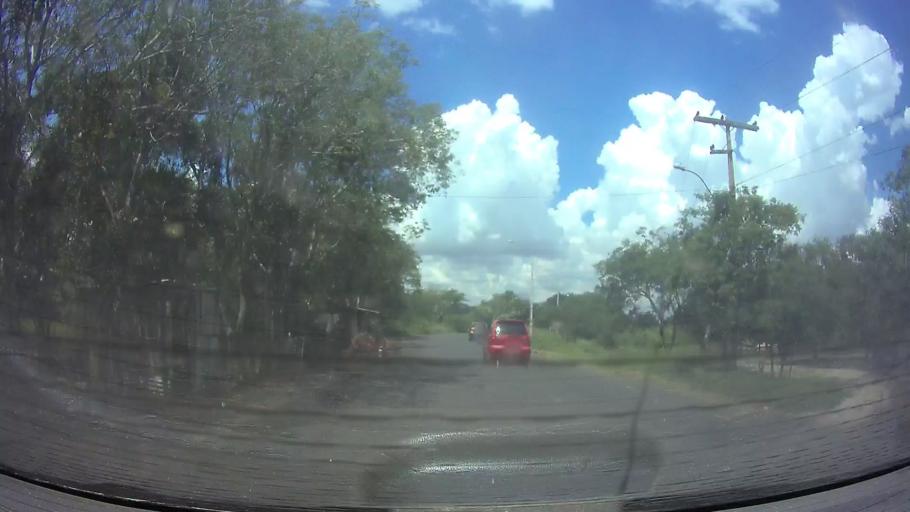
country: PY
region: Presidente Hayes
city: Nanawa
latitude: -25.2430
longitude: -57.6785
